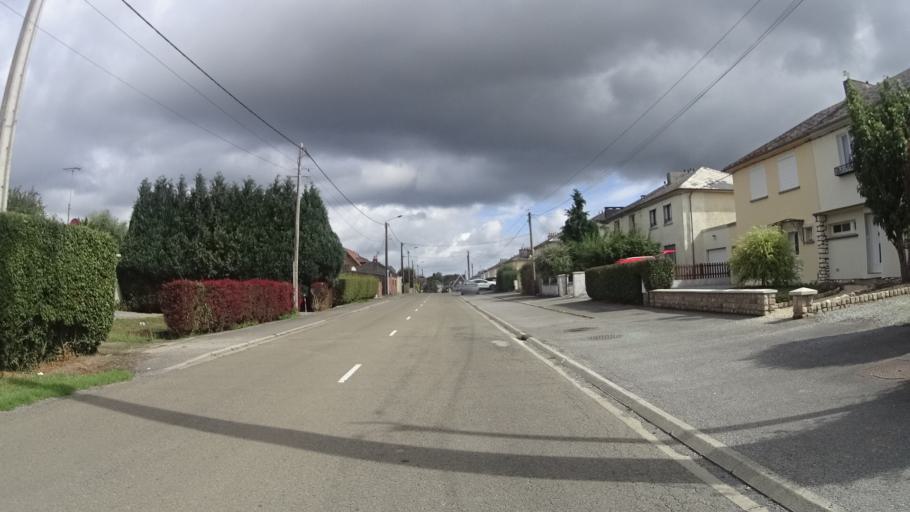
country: FR
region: Nord-Pas-de-Calais
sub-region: Departement du Nord
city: Landrecies
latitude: 50.1185
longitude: 3.6897
